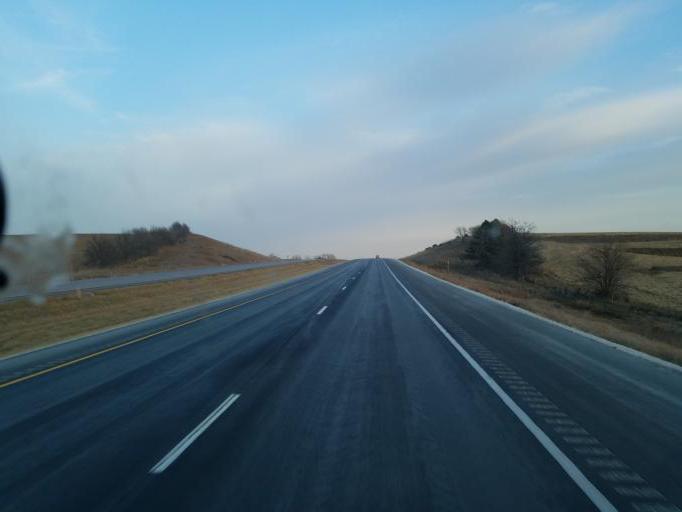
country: US
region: Iowa
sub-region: Harrison County
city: Missouri Valley
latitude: 41.4986
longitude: -95.7548
